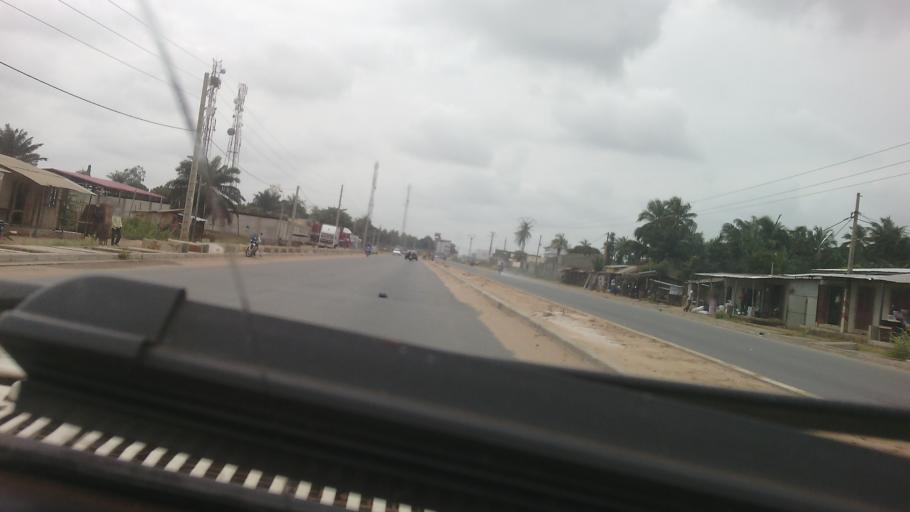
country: BJ
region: Atlantique
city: Hevie
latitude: 6.3850
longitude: 2.2043
